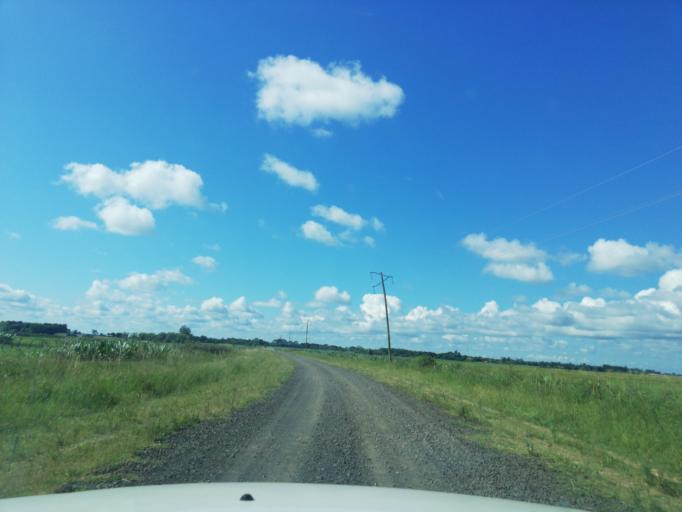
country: AR
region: Corrientes
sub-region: Departamento de San Miguel
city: San Miguel
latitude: -27.9744
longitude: -57.5805
